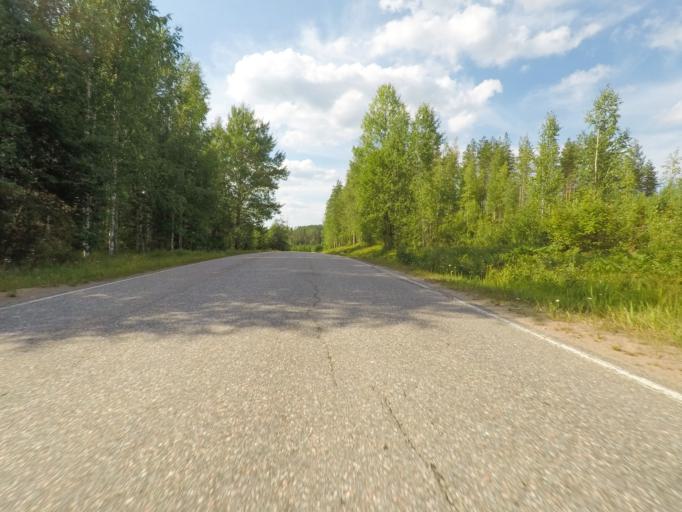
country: FI
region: Southern Savonia
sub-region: Mikkeli
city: Puumala
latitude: 61.6907
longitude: 28.2179
